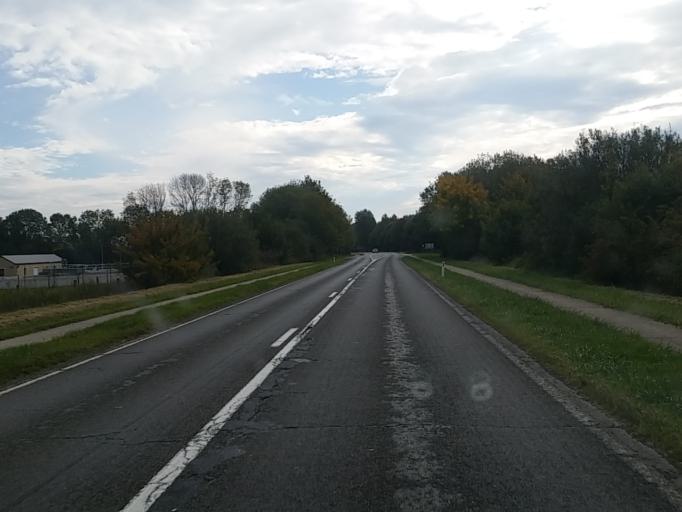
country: BE
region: Wallonia
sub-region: Province du Luxembourg
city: Etalle
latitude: 49.6727
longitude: 5.5787
